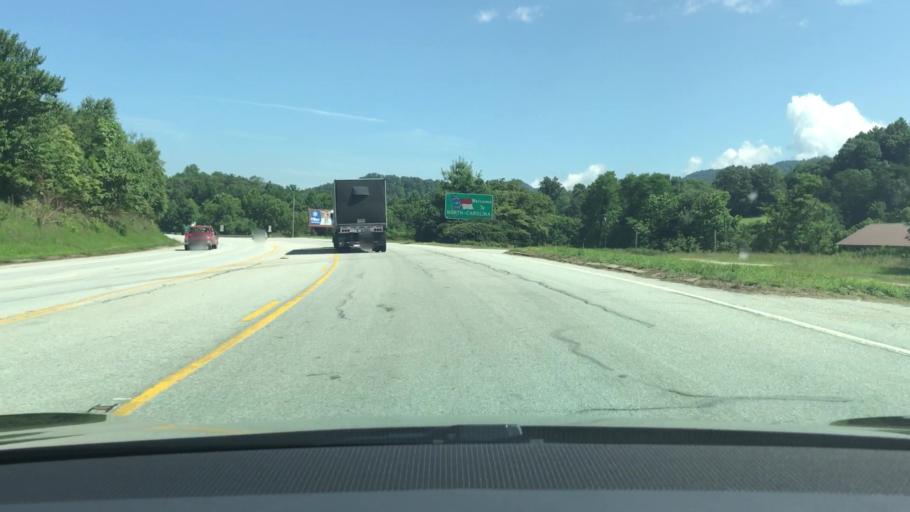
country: US
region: Georgia
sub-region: Rabun County
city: Mountain City
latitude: 34.9954
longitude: -83.3817
